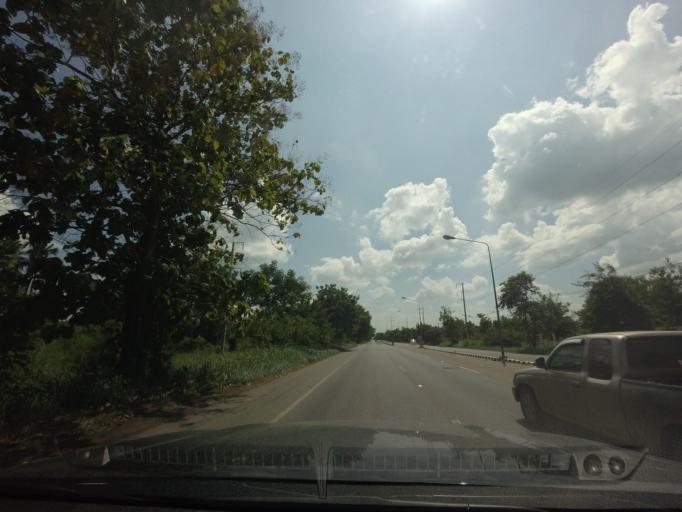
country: TH
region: Phetchabun
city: Nong Phai
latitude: 16.0403
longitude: 101.0793
